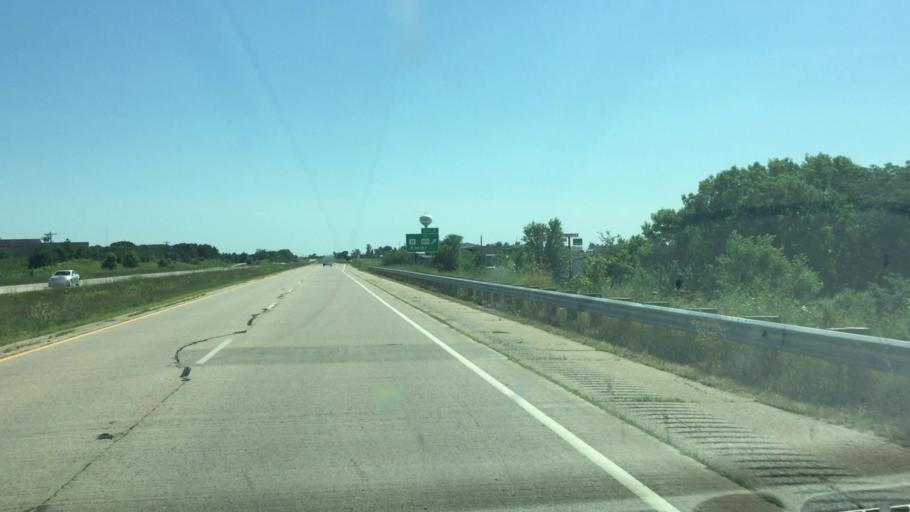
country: US
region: Wisconsin
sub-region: Grant County
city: Dickeyville
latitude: 42.5944
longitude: -90.5995
